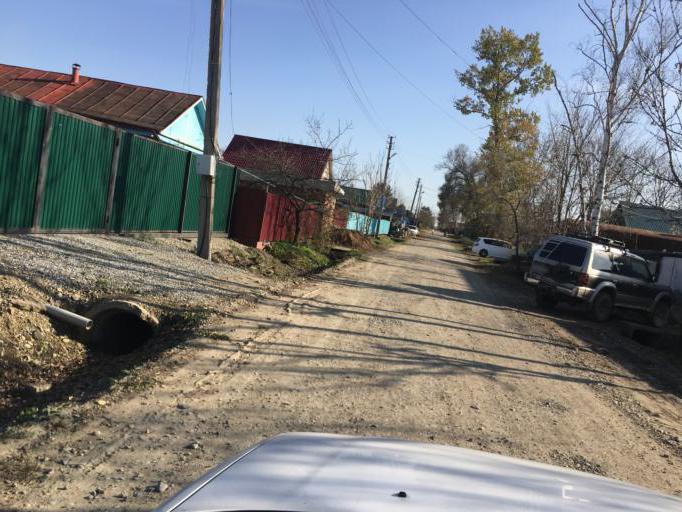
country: RU
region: Primorskiy
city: Dal'nerechensk
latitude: 45.9239
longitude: 133.7328
